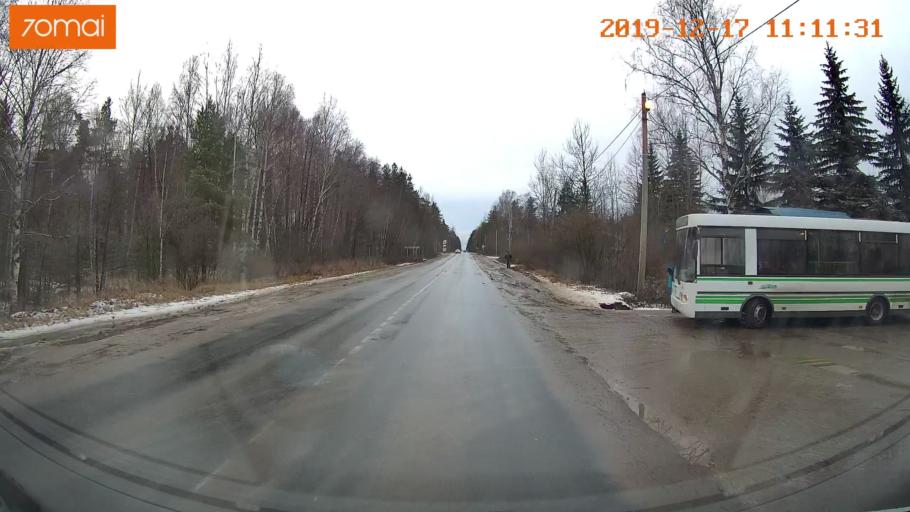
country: RU
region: Vladimir
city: Gus'-Khrustal'nyy
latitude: 55.5859
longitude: 40.6362
